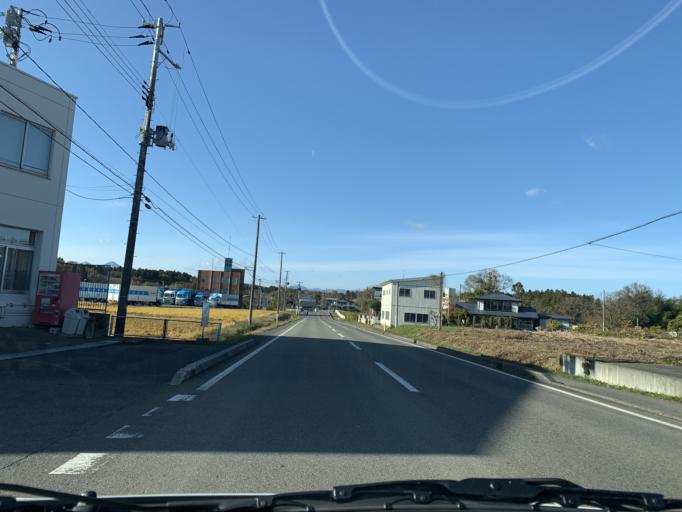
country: JP
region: Iwate
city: Mizusawa
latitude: 39.2036
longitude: 141.1138
